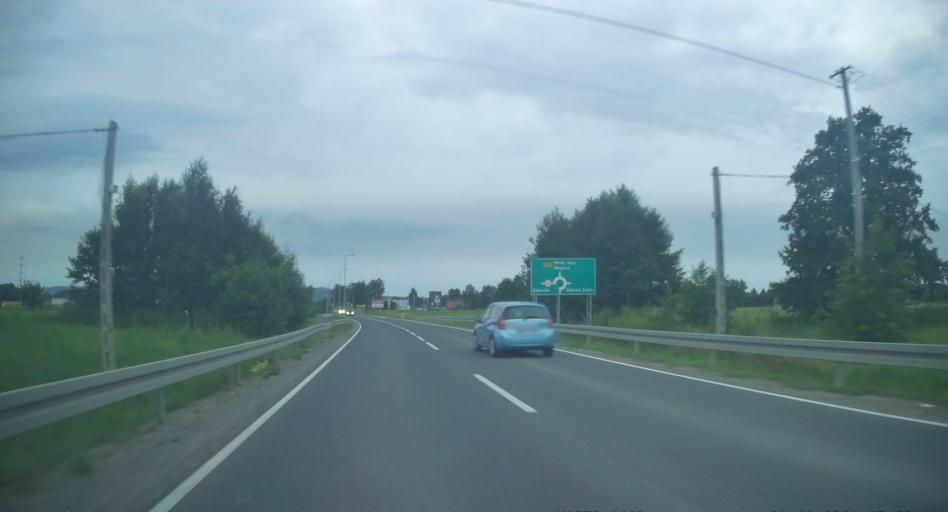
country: PL
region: Lesser Poland Voivodeship
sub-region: Powiat tarnowski
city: Wojnicz
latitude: 49.9766
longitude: 20.8422
